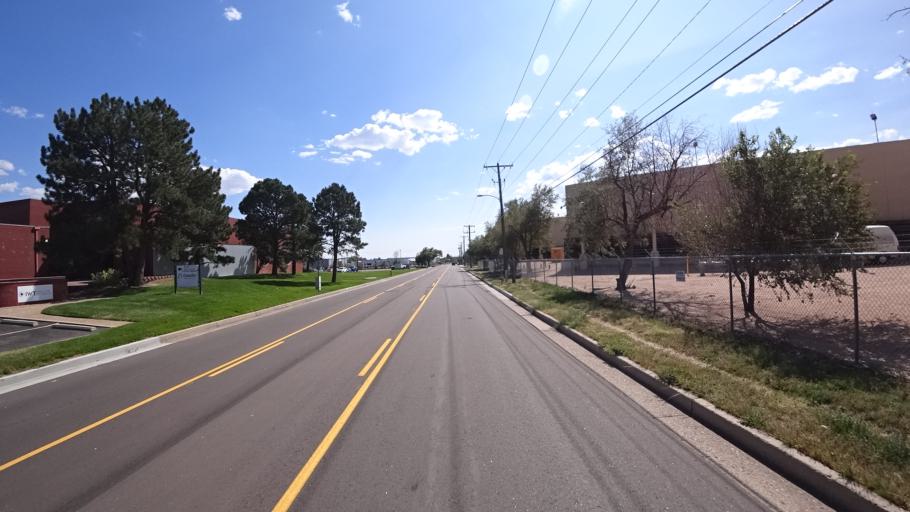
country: US
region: Colorado
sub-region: El Paso County
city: Colorado Springs
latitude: 38.8810
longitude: -104.8160
